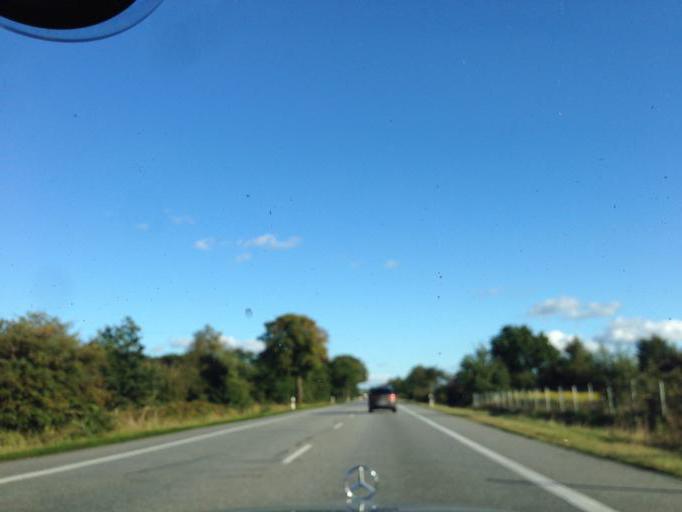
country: DE
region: Schleswig-Holstein
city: Wahlstedt
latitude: 53.9756
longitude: 10.2194
